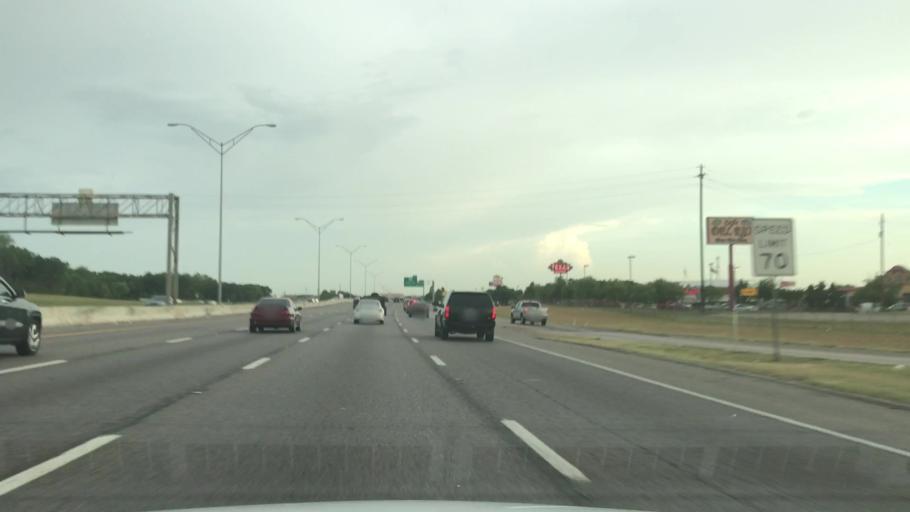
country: US
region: Texas
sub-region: Dallas County
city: Mesquite
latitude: 32.7879
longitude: -96.6247
